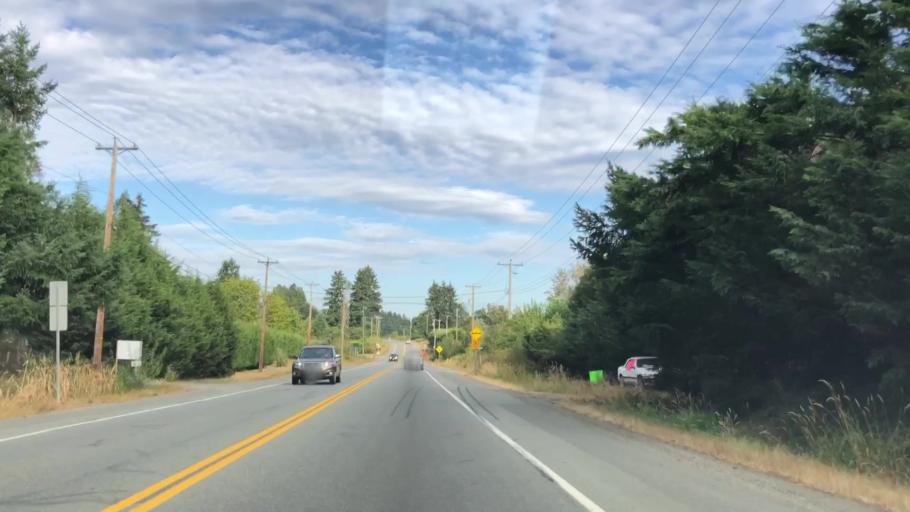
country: CA
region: British Columbia
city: Duncan
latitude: 48.8142
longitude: -123.7332
